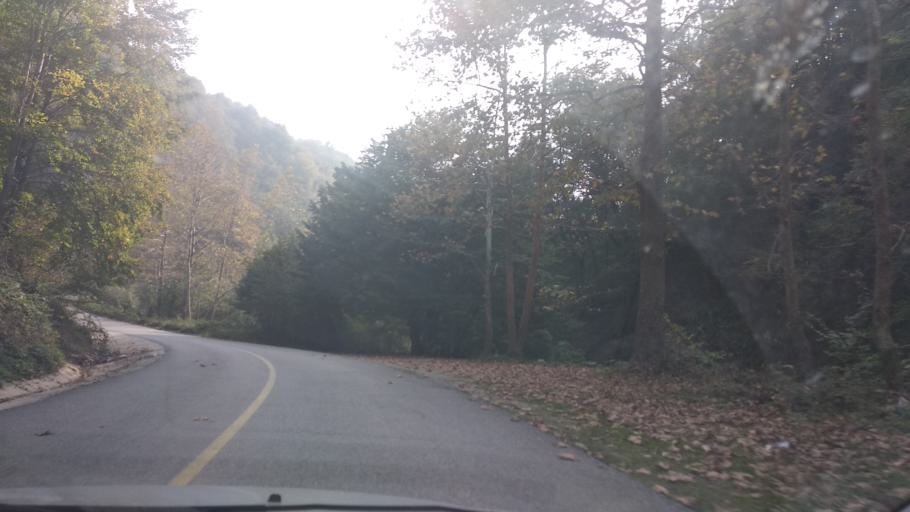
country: TR
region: Duzce
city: Kaynasli
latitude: 40.7114
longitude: 31.2665
